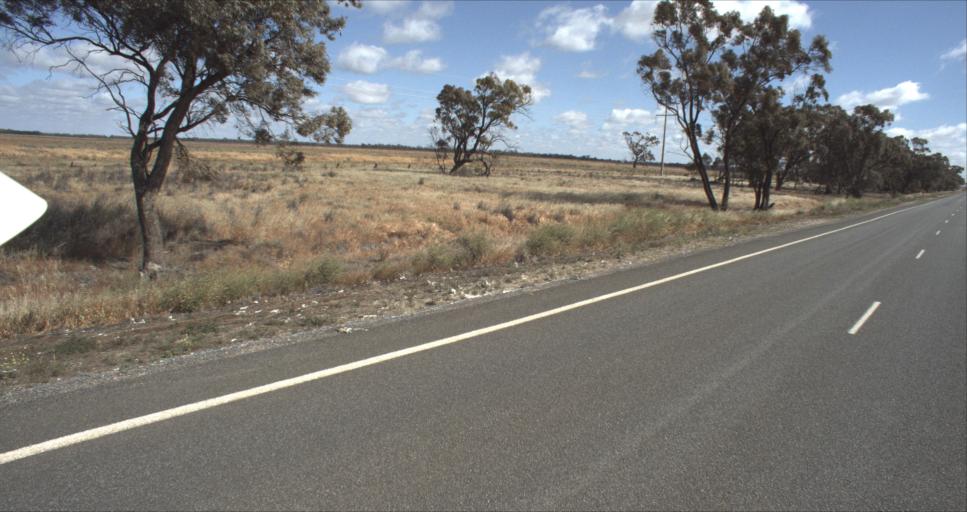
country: AU
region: New South Wales
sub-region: Murrumbidgee Shire
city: Darlington Point
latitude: -34.5609
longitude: 146.1690
